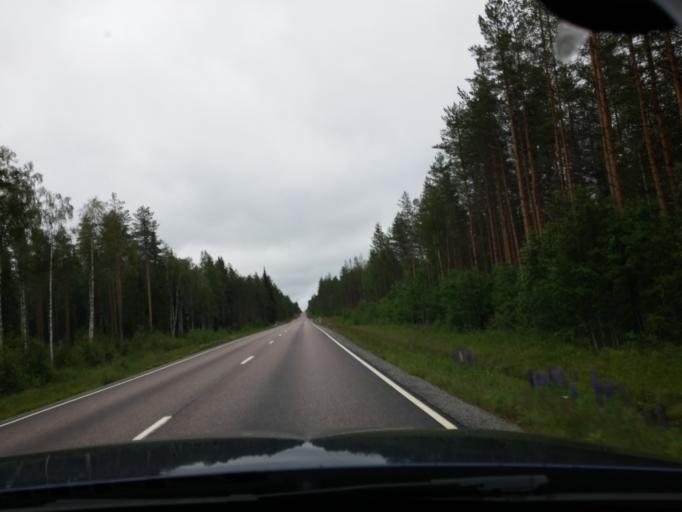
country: FI
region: Central Finland
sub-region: Saarijaervi-Viitasaari
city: Pylkoenmaeki
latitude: 62.5948
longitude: 24.6094
